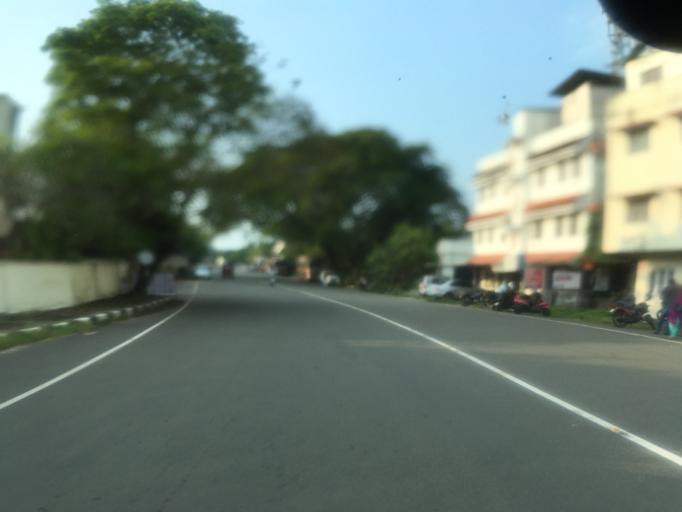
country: IN
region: Kerala
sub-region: Ernakulam
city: Cochin
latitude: 9.9623
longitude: 76.2665
